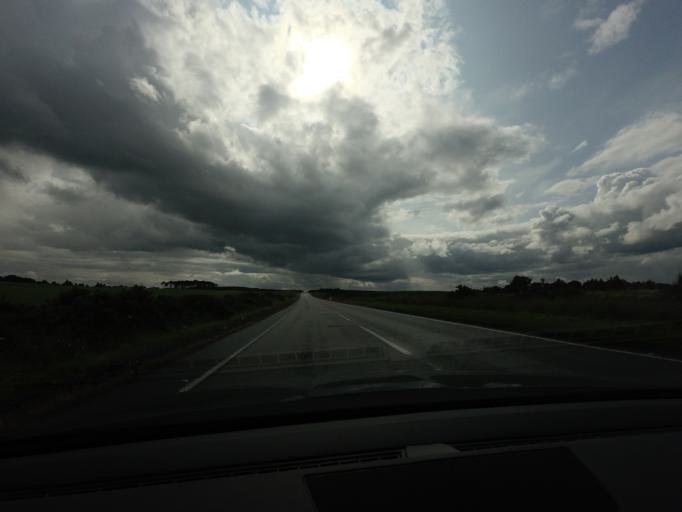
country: GB
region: Scotland
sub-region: Highland
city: Nairn
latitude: 57.5537
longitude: -3.9797
